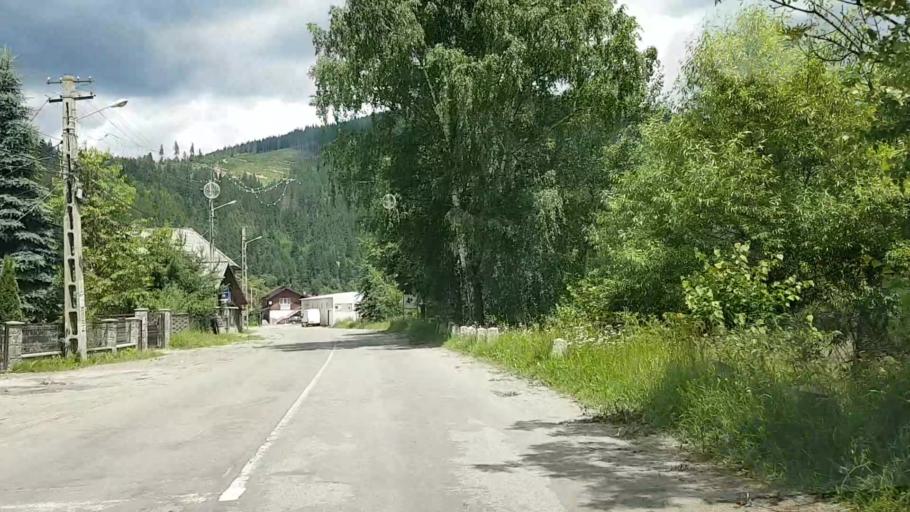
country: RO
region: Suceava
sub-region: Comuna Brosteni
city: Brosteni
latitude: 47.2383
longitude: 25.6981
